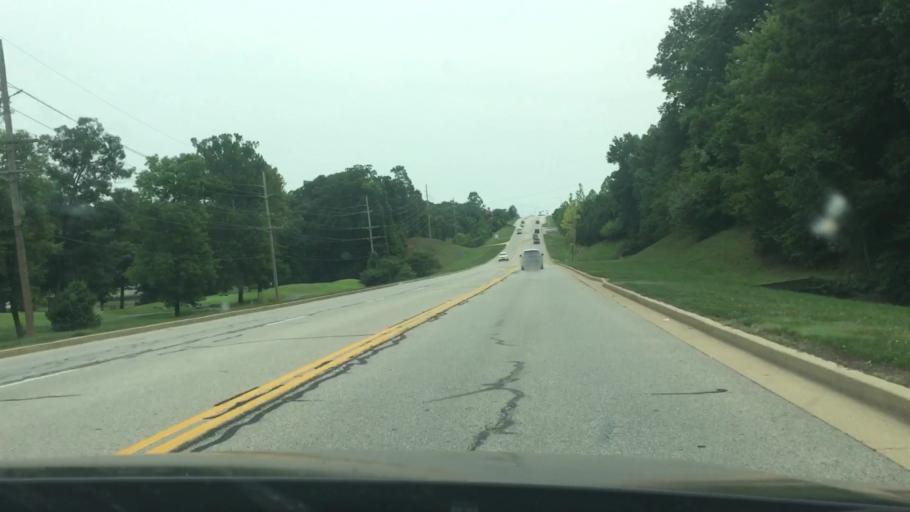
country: US
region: Missouri
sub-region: Miller County
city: Lake Ozark
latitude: 38.1917
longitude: -92.6542
